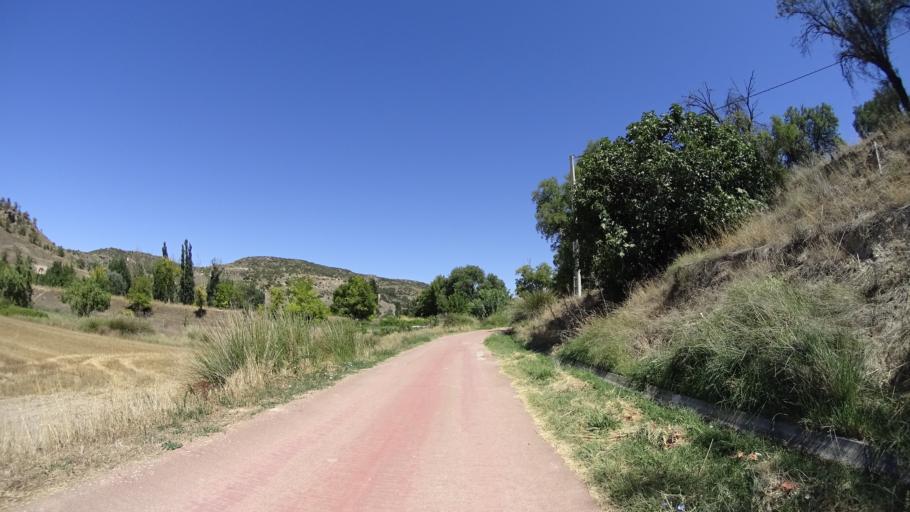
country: ES
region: Madrid
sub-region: Provincia de Madrid
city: Carabana
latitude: 40.2858
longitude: -3.2001
